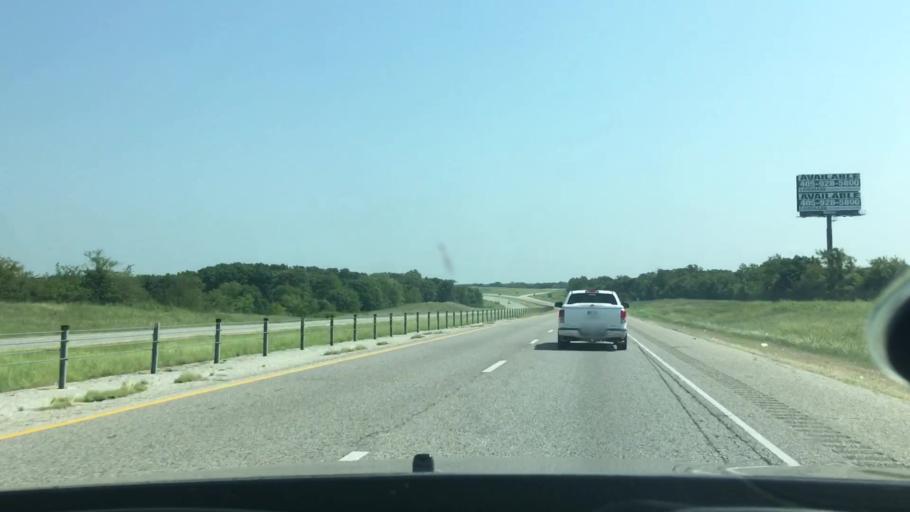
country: US
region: Oklahoma
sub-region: Bryan County
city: Durant
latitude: 34.0433
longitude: -96.3664
